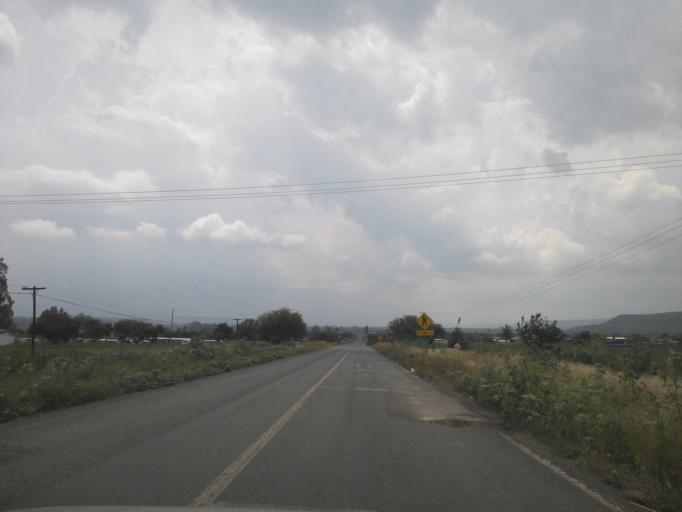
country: MX
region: Guanajuato
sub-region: San Francisco del Rincon
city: San Ignacio de Hidalgo
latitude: 20.8917
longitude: -101.9457
